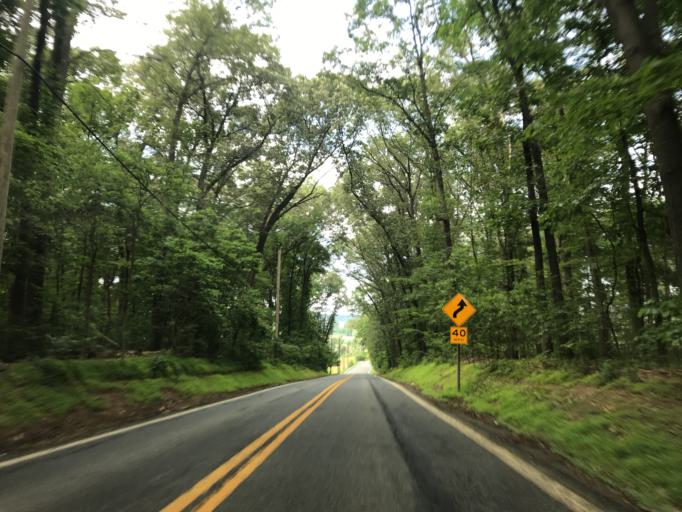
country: US
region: Pennsylvania
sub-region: York County
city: Susquehanna Trails
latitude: 39.6756
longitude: -76.4100
